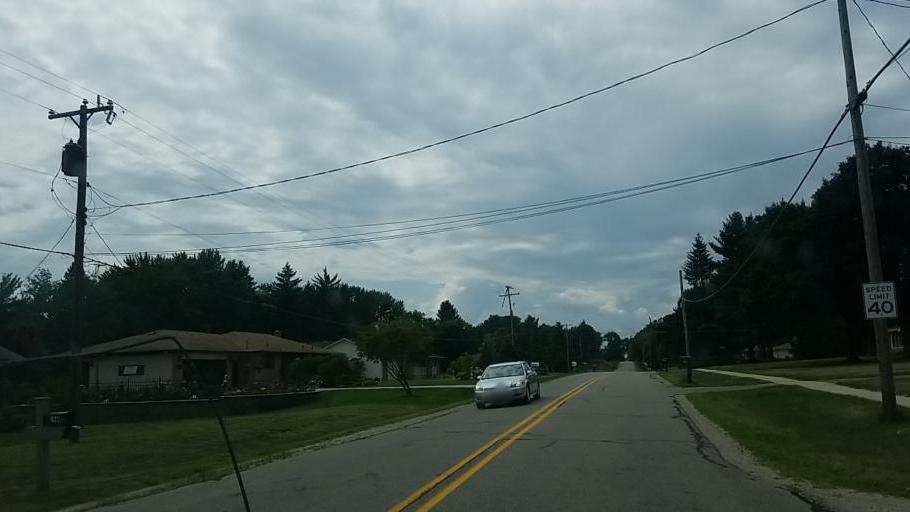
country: US
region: Michigan
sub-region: Kent County
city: Walker
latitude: 43.0010
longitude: -85.7435
